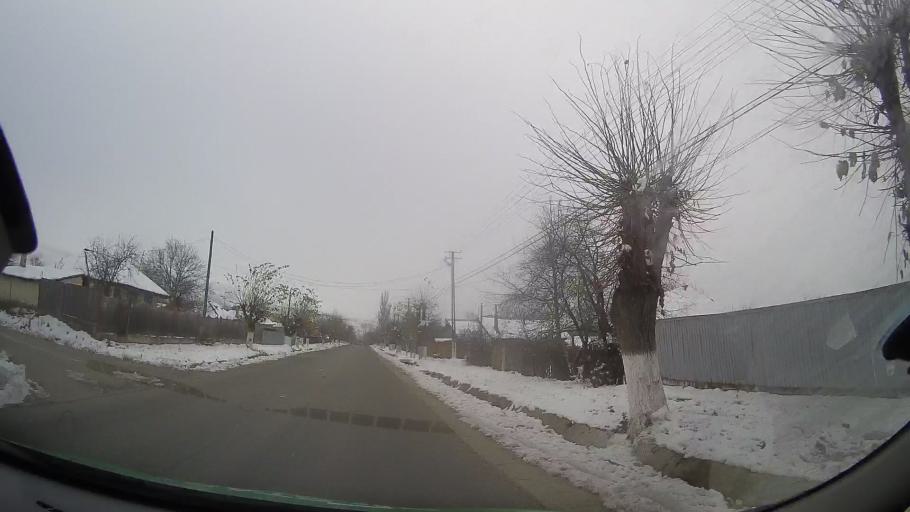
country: RO
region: Bacau
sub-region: Comuna Glavanesti
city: Frumuselu
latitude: 46.2991
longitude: 27.2984
